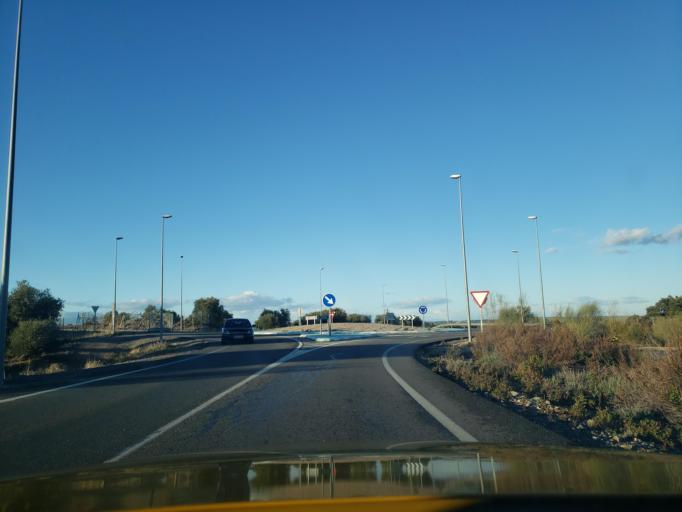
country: ES
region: Castille-La Mancha
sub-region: Province of Toledo
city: Toledo
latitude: 39.8359
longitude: -4.0196
